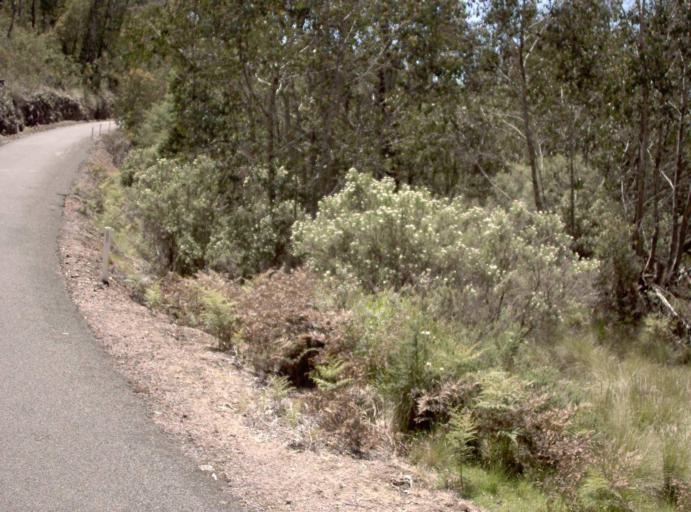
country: AU
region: New South Wales
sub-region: Snowy River
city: Jindabyne
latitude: -37.1184
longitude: 148.2401
